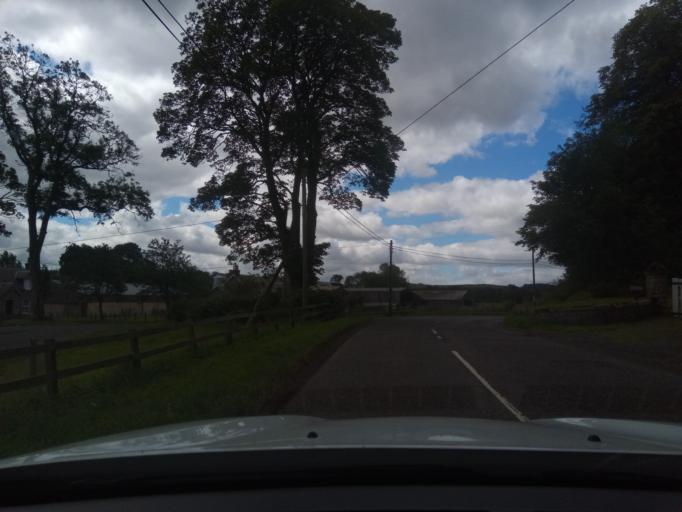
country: GB
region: Scotland
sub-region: The Scottish Borders
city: Selkirk
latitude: 55.5412
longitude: -2.8724
